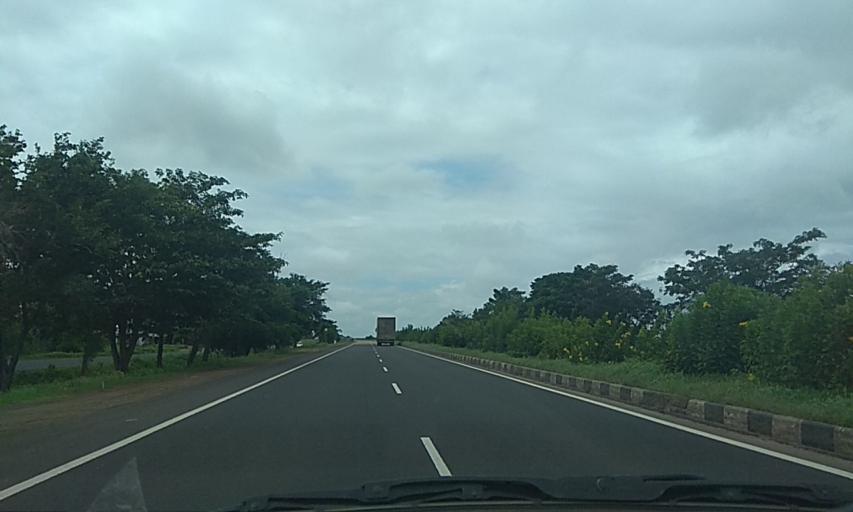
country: IN
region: Maharashtra
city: Nipani
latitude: 16.3860
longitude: 74.3879
